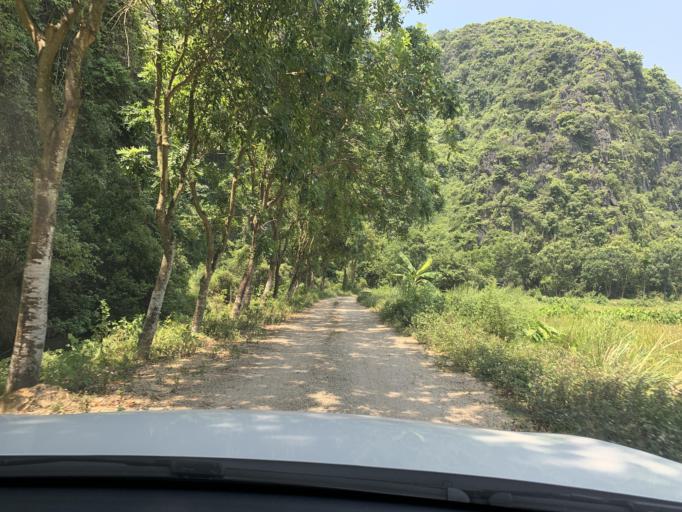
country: VN
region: Ninh Binh
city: Thanh Pho Ninh Binh
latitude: 20.2221
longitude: 105.9295
